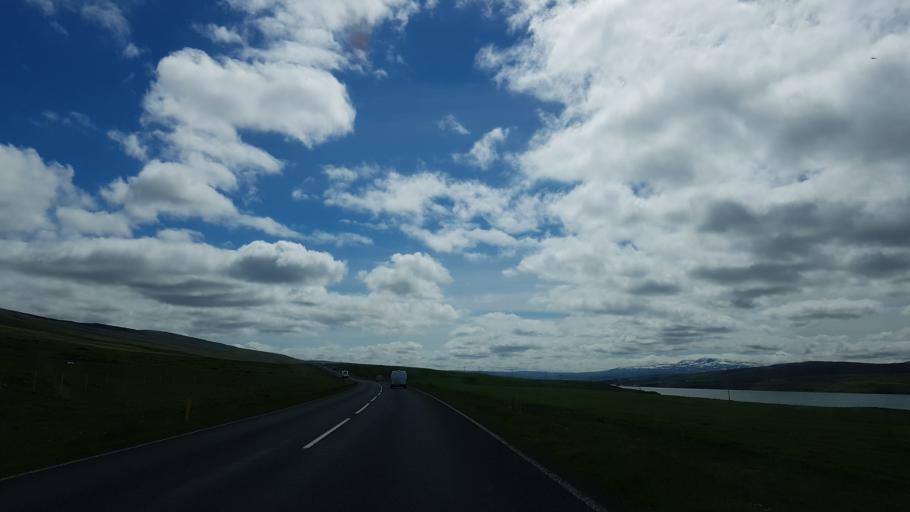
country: IS
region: West
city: Borgarnes
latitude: 65.2428
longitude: -21.0888
